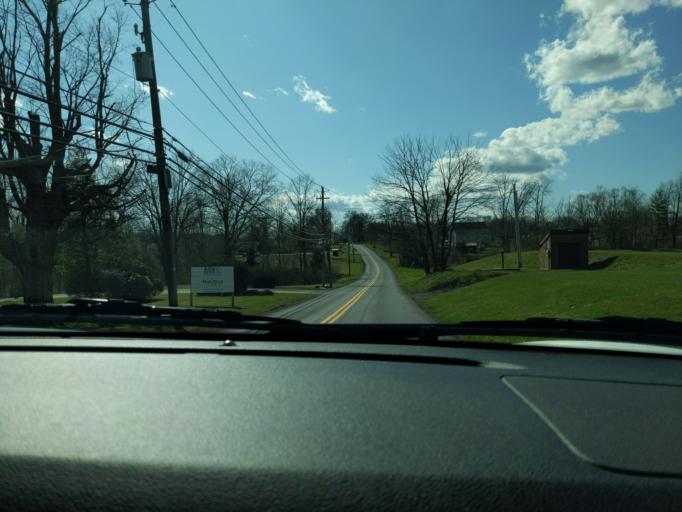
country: US
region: Pennsylvania
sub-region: Bucks County
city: Quakertown
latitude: 40.4388
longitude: -75.3836
